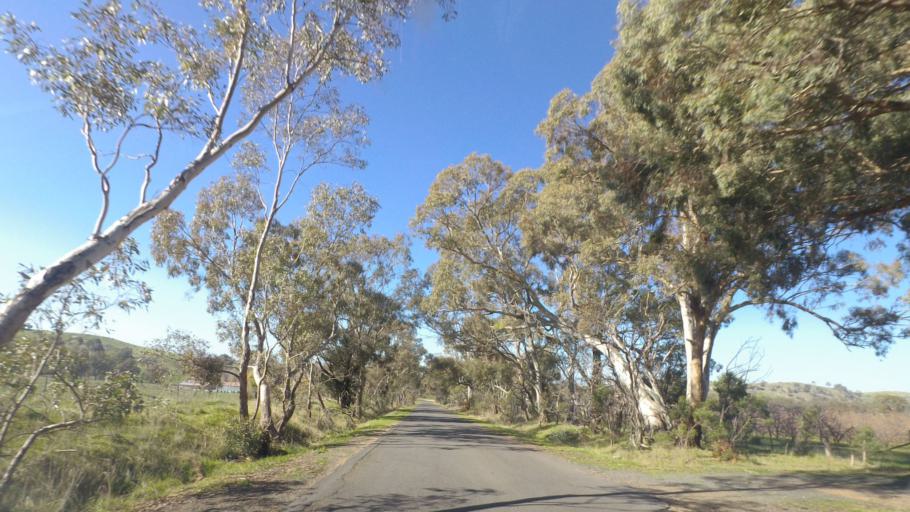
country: AU
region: Victoria
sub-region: Mount Alexander
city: Castlemaine
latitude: -36.9684
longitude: 144.3127
